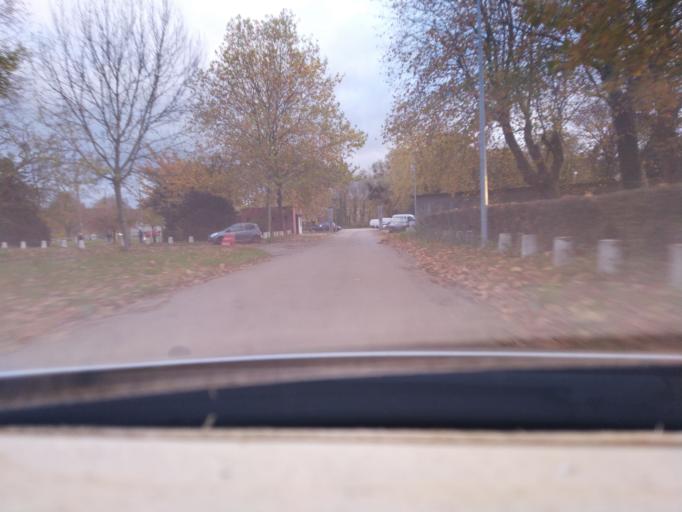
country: FR
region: Haute-Normandie
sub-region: Departement de la Seine-Maritime
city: Yainville
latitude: 49.4585
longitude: 0.8197
